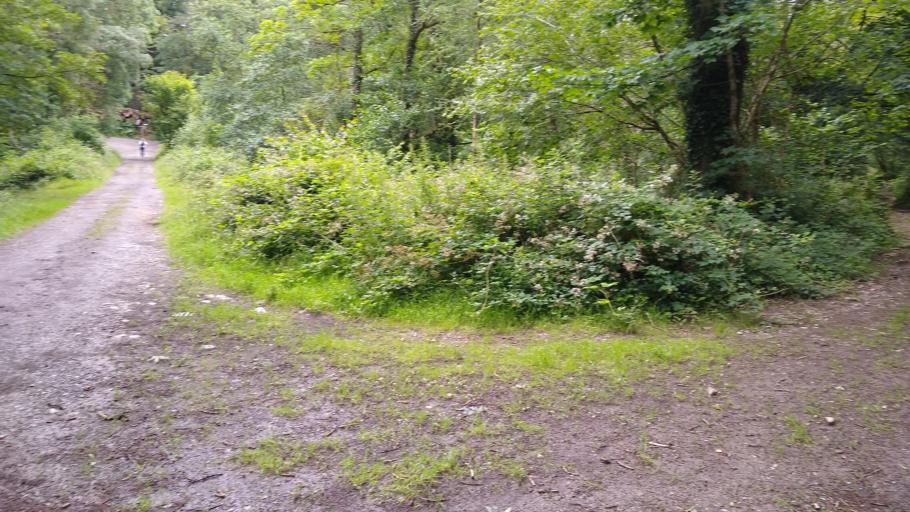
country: GB
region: England
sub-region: Devon
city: Combe Martin
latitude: 51.1380
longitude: -3.9905
